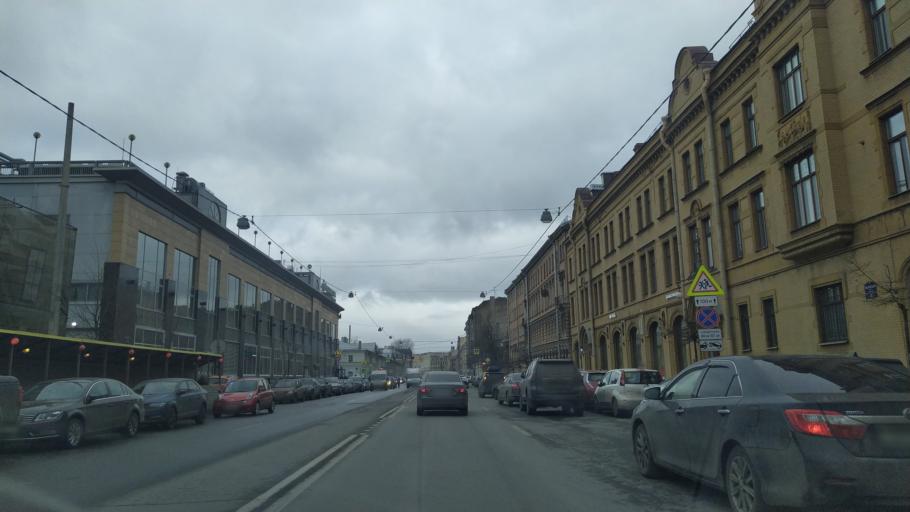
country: RU
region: St.-Petersburg
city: Centralniy
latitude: 59.9187
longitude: 30.3409
